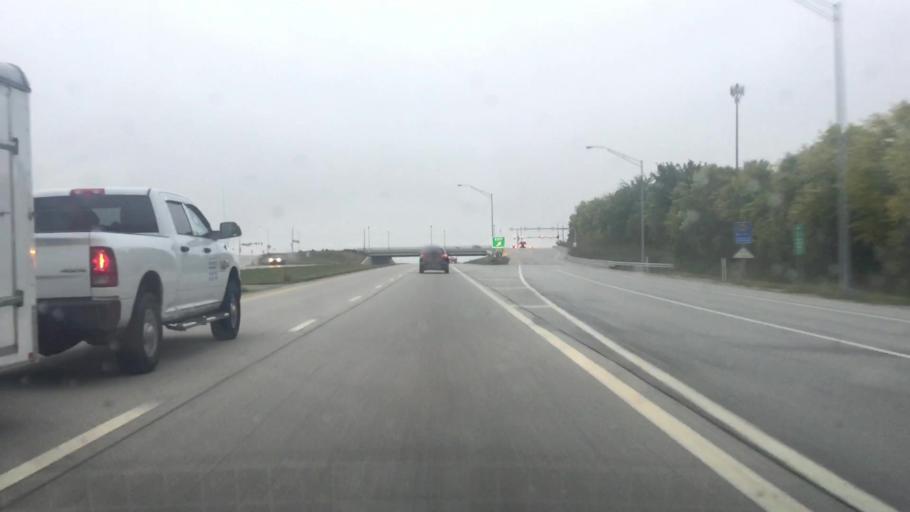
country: US
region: Kansas
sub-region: Johnson County
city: Lenexa
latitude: 38.8437
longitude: -94.6767
